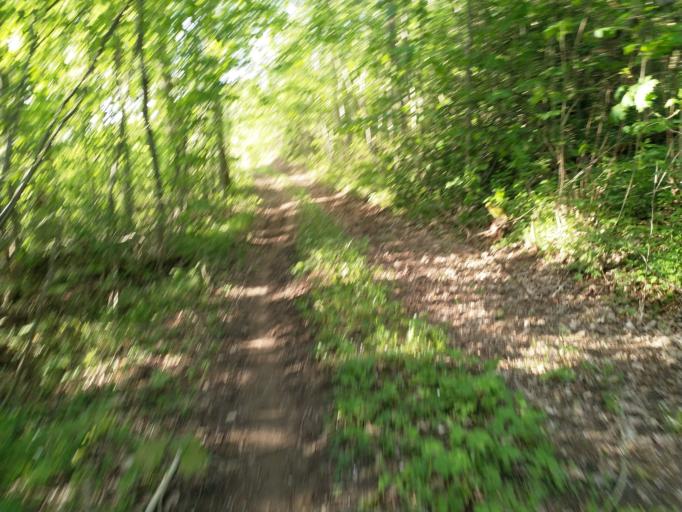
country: LV
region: Kuldigas Rajons
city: Kuldiga
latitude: 56.8584
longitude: 21.8597
